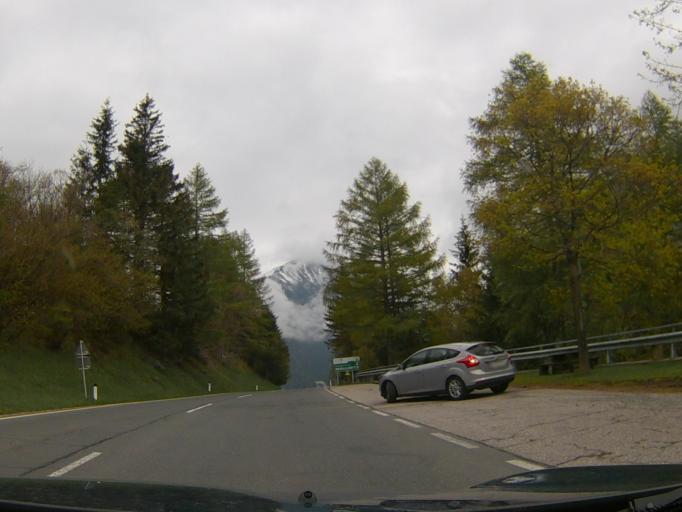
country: AT
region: Carinthia
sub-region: Politischer Bezirk Spittal an der Drau
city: Obervellach
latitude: 46.9713
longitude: 13.1816
